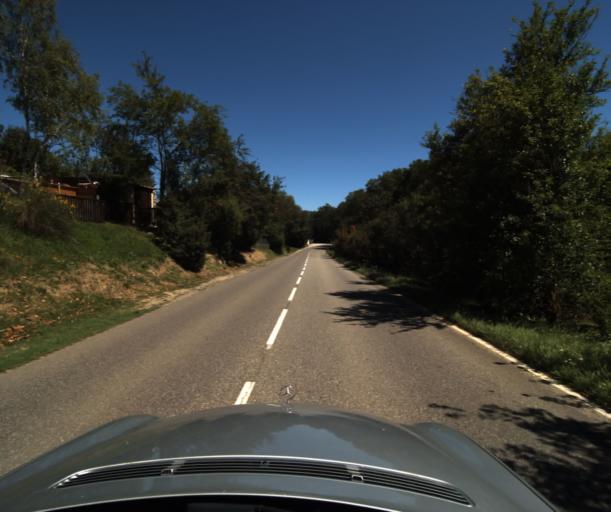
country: FR
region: Midi-Pyrenees
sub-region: Departement de l'Ariege
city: Belesta
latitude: 42.9558
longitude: 1.9036
